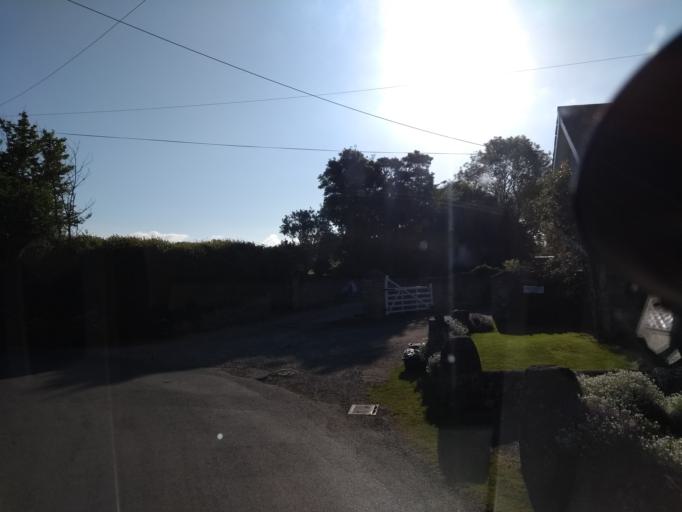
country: GB
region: England
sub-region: Somerset
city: Creech Saint Michael
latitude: 51.0048
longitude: -3.0482
